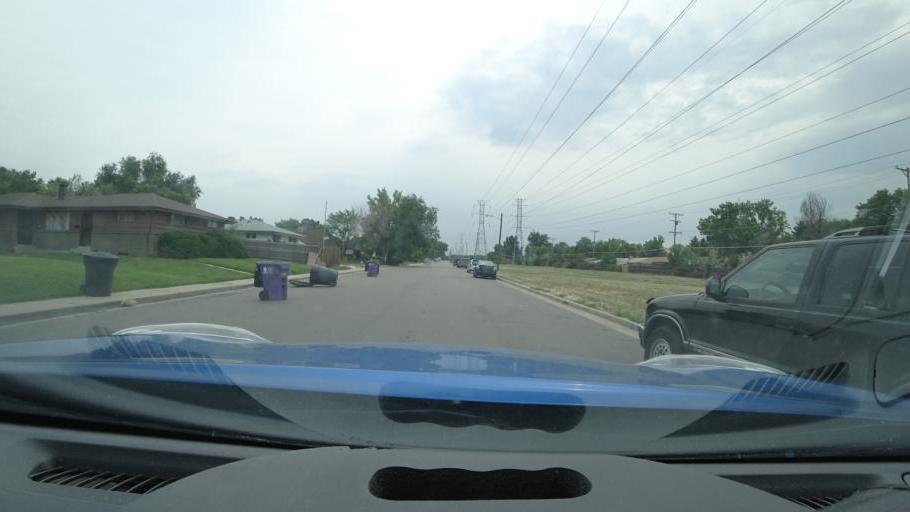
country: US
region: Colorado
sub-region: Arapahoe County
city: Glendale
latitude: 39.7026
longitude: -104.9176
